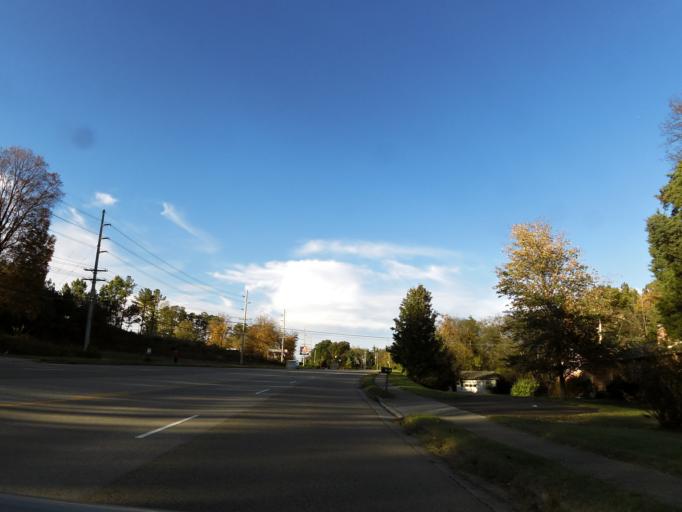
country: US
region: Tennessee
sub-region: Blount County
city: Louisville
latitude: 35.8741
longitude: -84.0649
